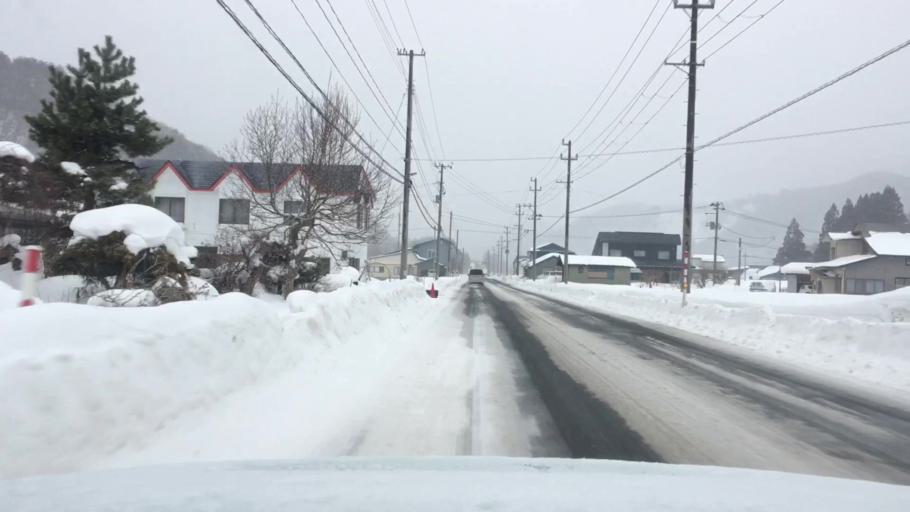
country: JP
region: Akita
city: Hanawa
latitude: 40.0564
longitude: 141.0097
